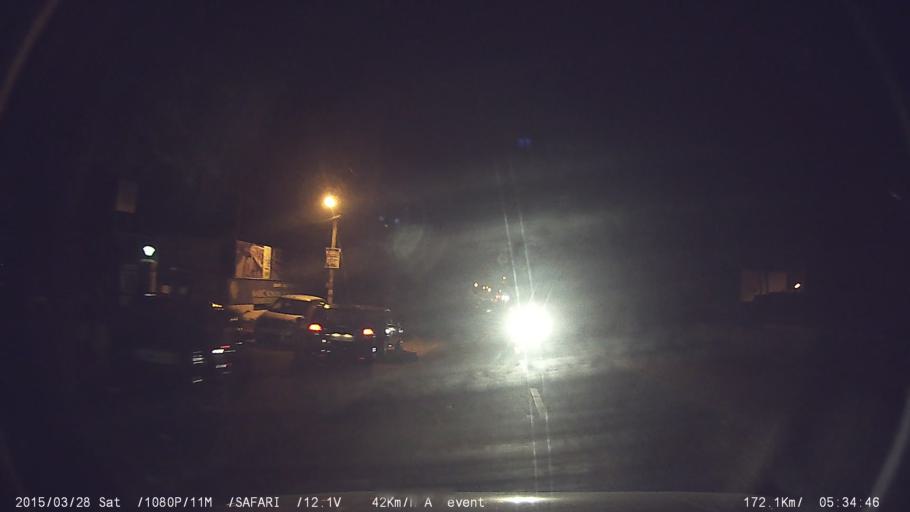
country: IN
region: Karnataka
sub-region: Bangalore Urban
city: Bangalore
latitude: 12.8651
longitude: 77.5915
